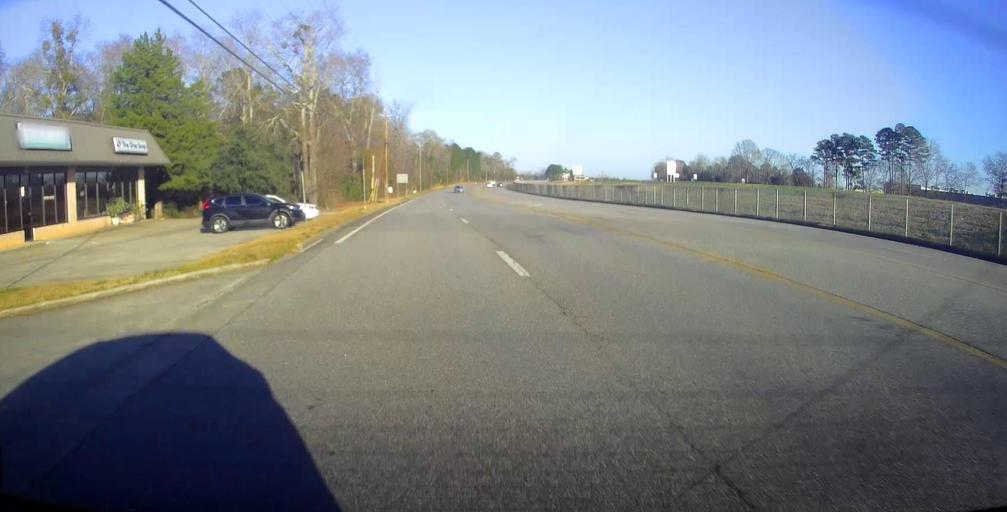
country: US
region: Georgia
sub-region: Dougherty County
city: Albany
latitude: 31.6236
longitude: -84.2264
